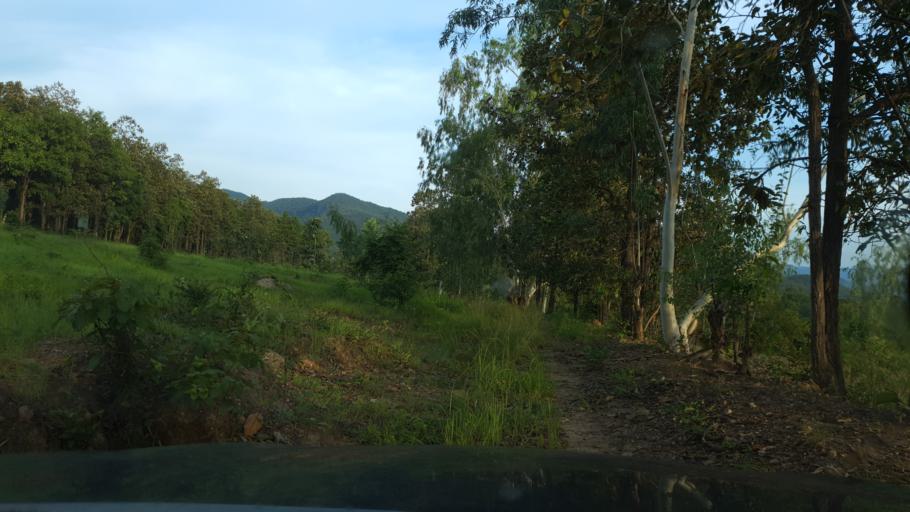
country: TH
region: Lamphun
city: Ban Thi
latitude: 18.6703
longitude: 99.1690
